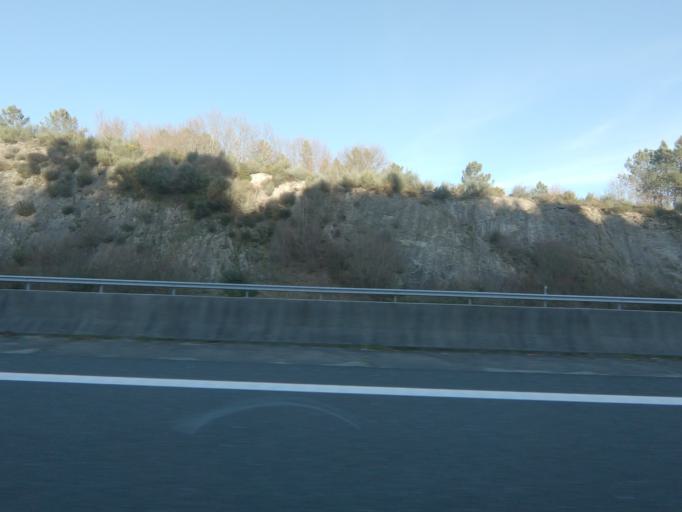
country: ES
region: Galicia
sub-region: Provincia de Ourense
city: Pinor
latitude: 42.4894
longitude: -8.0236
